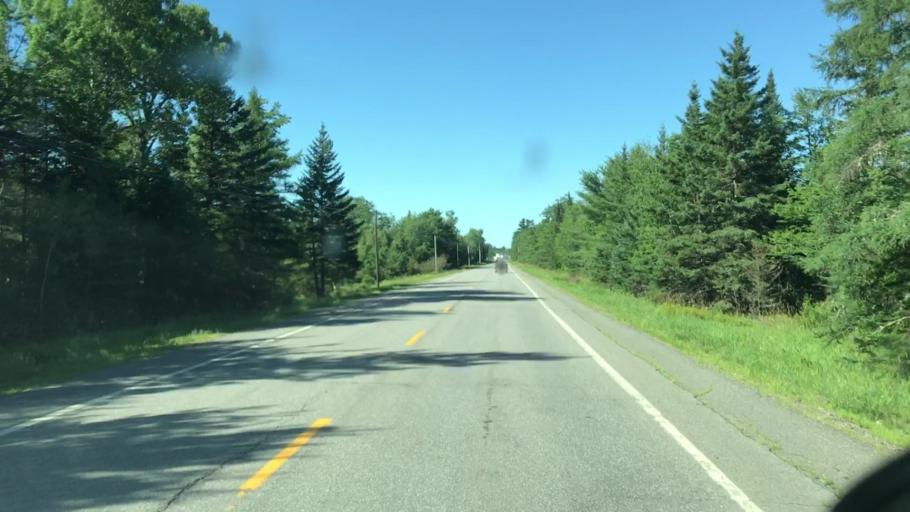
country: US
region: Maine
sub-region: Penobscot County
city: Enfield
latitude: 45.3056
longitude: -68.6125
